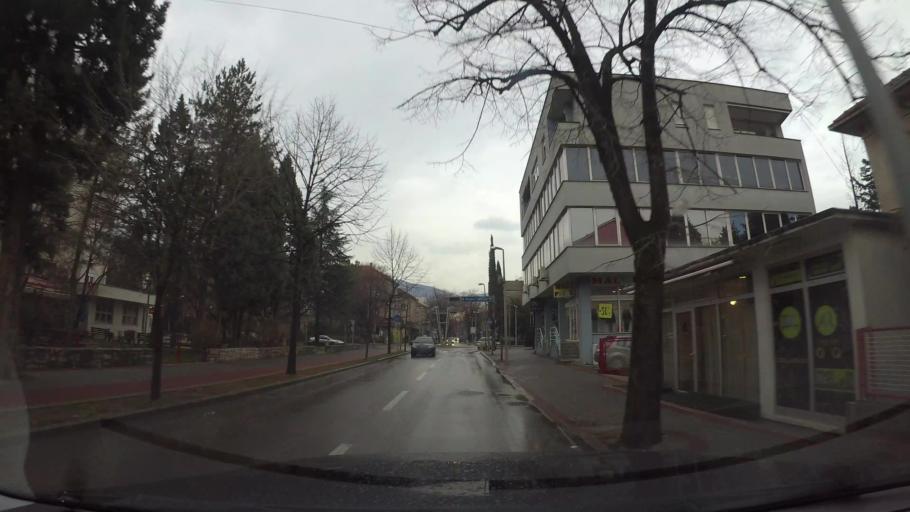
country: BA
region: Federation of Bosnia and Herzegovina
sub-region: Hercegovacko-Bosanski Kanton
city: Mostar
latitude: 43.3440
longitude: 17.8037
